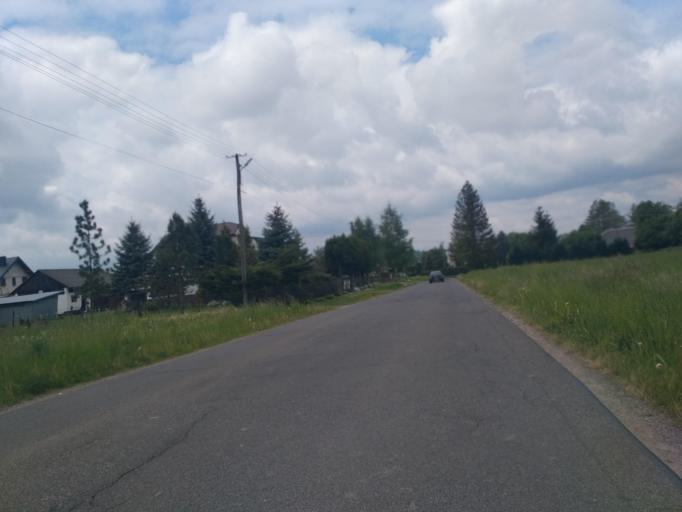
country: PL
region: Subcarpathian Voivodeship
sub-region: Powiat krosnienski
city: Chorkowka
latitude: 49.6650
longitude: 21.6200
